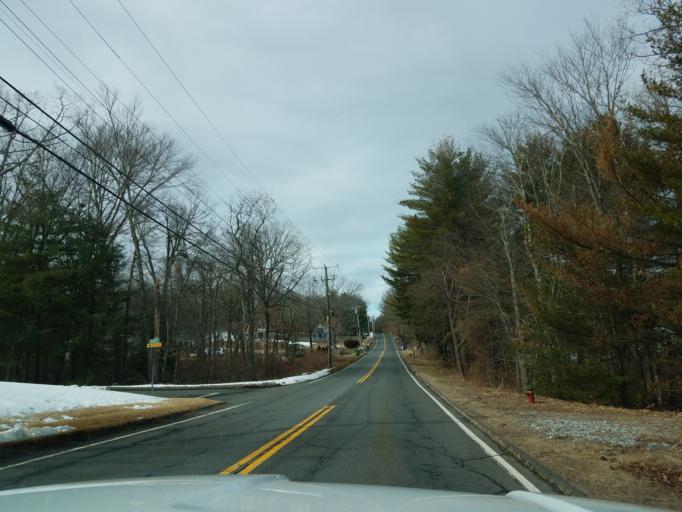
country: US
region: Connecticut
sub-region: Hartford County
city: Weatogue
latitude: 41.8026
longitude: -72.8459
